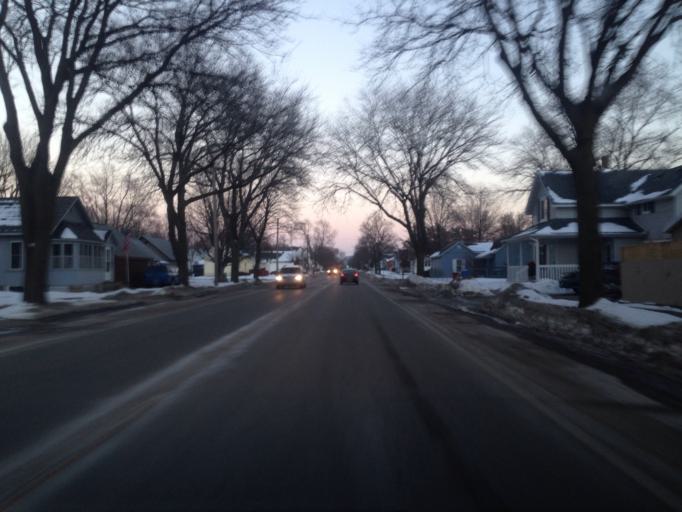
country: US
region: Minnesota
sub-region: Winona County
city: Winona
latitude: 44.0464
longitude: -91.6547
